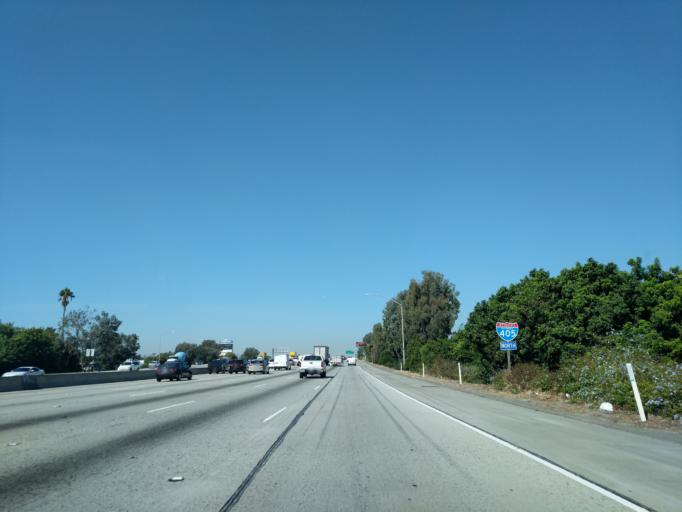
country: US
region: California
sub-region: Los Angeles County
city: Signal Hill
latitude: 33.8067
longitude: -118.1473
